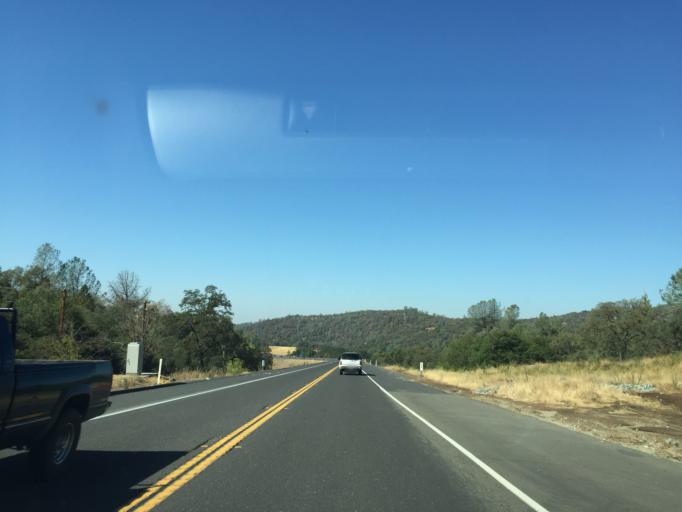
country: US
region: California
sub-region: Tuolumne County
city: East Sonora
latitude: 37.9811
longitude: -120.3251
